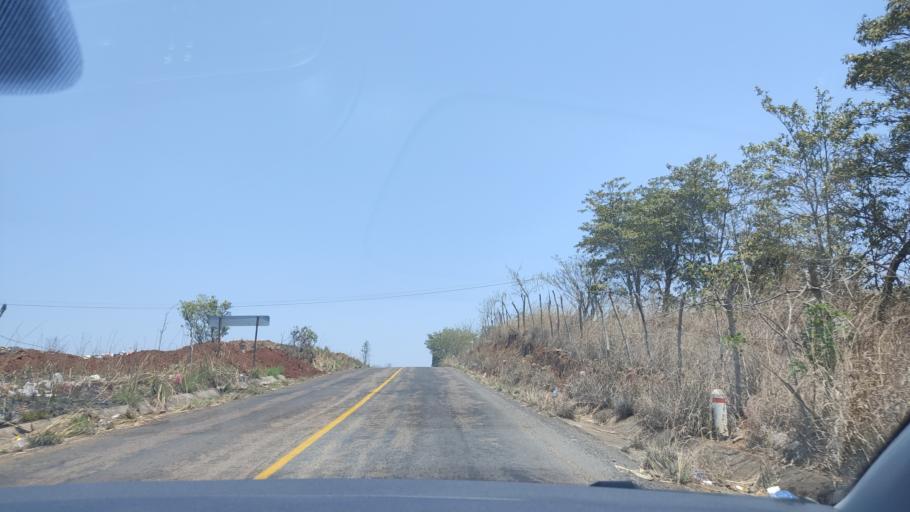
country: MX
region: Nayarit
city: Puga
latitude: 21.5750
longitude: -104.7597
